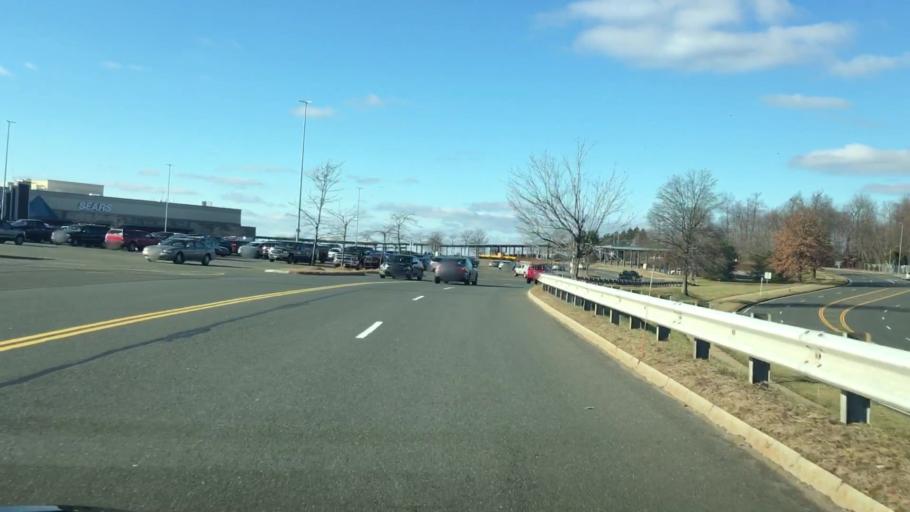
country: US
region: Connecticut
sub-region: Hartford County
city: Manchester
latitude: 41.8086
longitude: -72.5442
